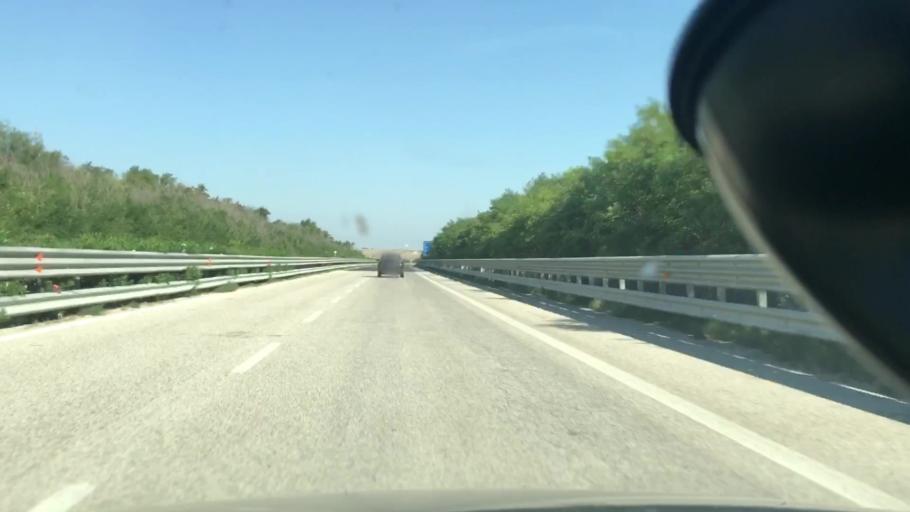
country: IT
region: Apulia
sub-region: Provincia di Foggia
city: Ordona
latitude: 41.2930
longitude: 15.5540
